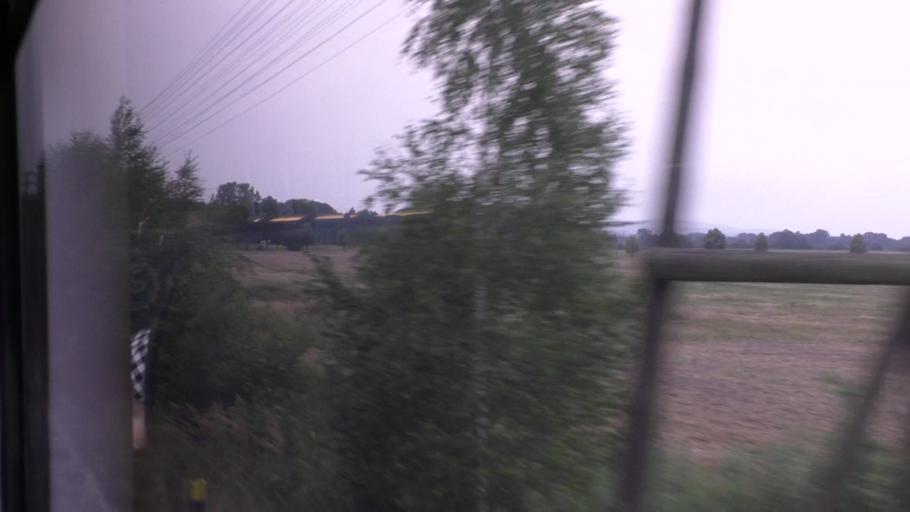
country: DE
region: Saxony
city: Horka
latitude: 51.2836
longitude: 14.9029
